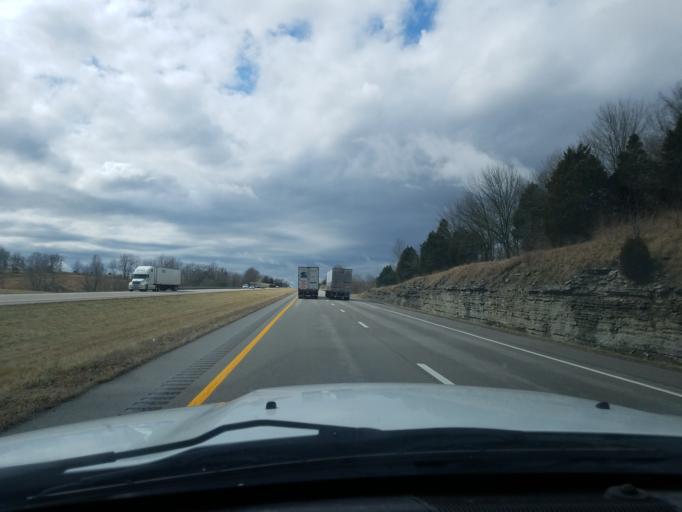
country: US
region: Kentucky
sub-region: Montgomery County
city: Mount Sterling
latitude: 38.0957
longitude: -83.8648
